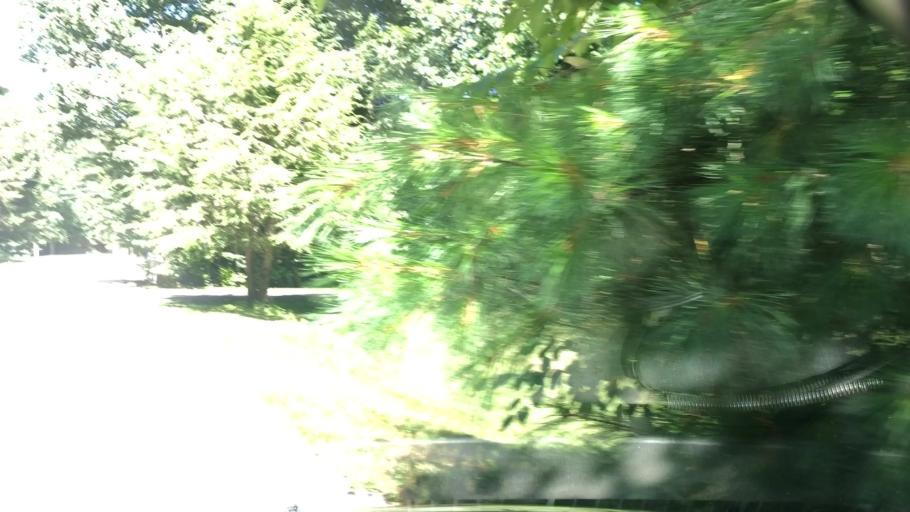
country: US
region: New Hampshire
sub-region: Hillsborough County
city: Milford
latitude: 42.8552
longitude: -71.5876
